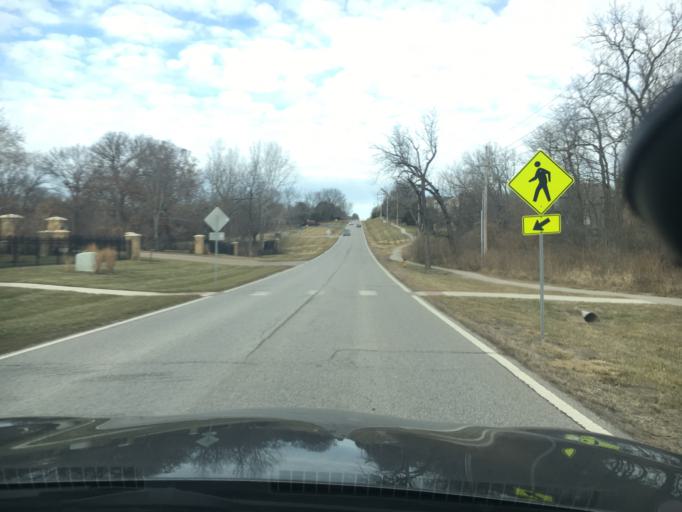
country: US
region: Missouri
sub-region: Jackson County
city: Grandview
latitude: 38.8626
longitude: -94.6305
